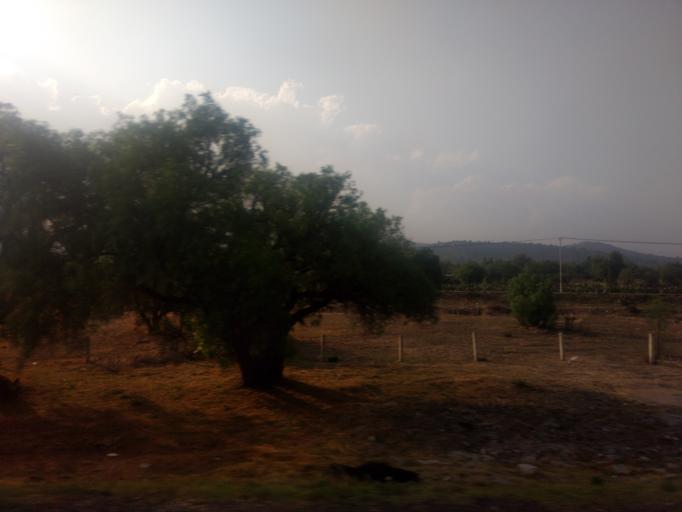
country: MX
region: Mexico
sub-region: Axapusco
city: Colonia los Remedios
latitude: 19.7250
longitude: -98.7826
